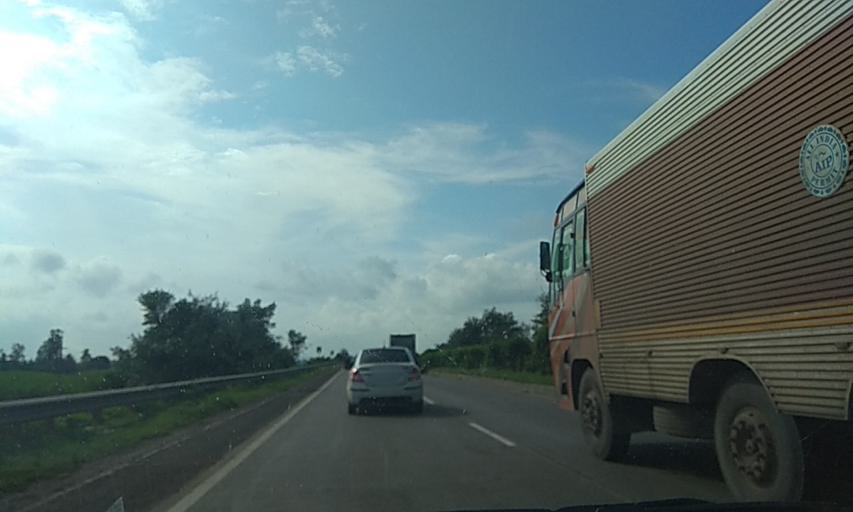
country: IN
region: Maharashtra
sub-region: Kolhapur
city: Kodoli
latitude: 16.8913
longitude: 74.2938
